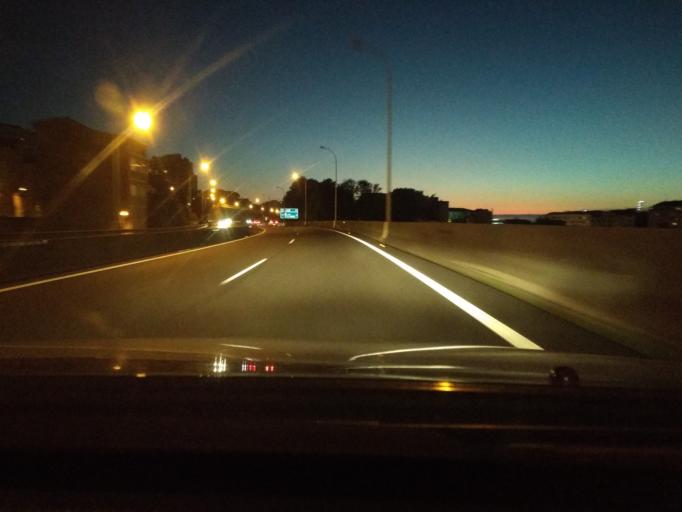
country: ES
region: Galicia
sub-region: Provincia de Pontevedra
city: Vigo
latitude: 42.2456
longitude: -8.6978
